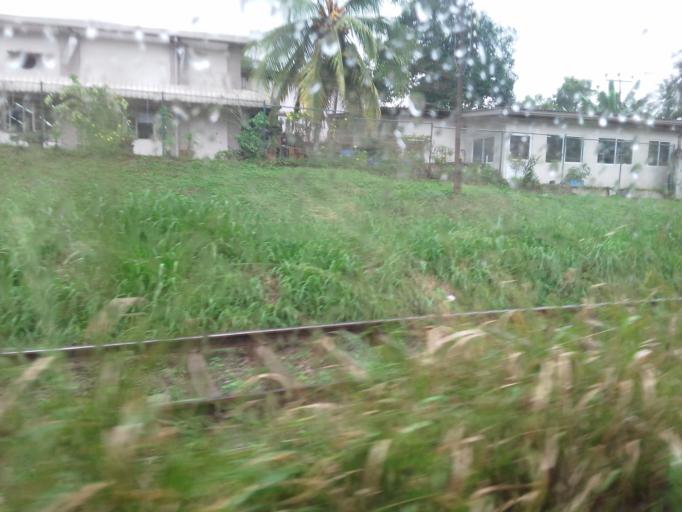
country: LK
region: Western
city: Homagama
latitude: 6.8433
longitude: 80.0579
